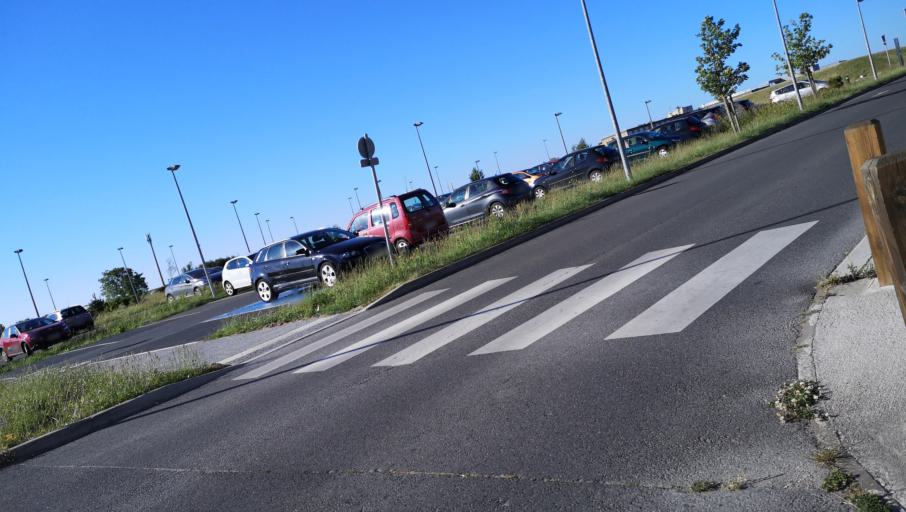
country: FR
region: Centre
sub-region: Departement du Loiret
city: Saran
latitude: 47.9392
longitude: 1.8793
